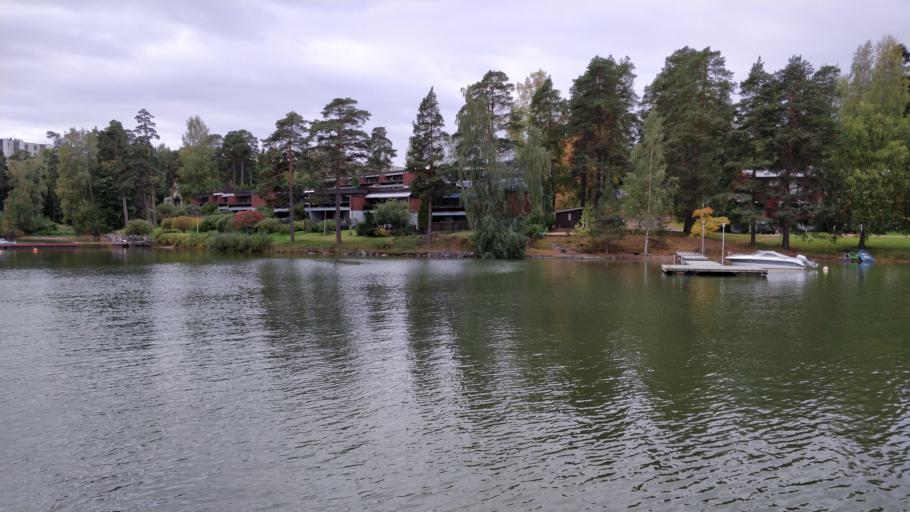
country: FI
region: Uusimaa
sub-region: Helsinki
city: Vantaa
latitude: 60.1859
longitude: 25.0636
